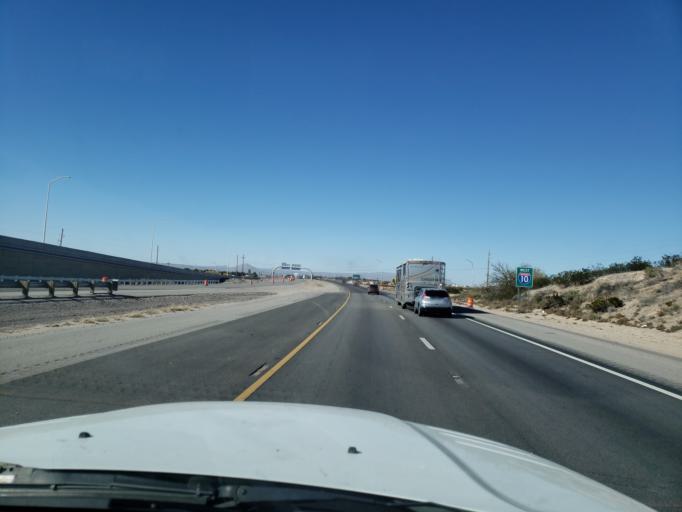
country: US
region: New Mexico
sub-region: Dona Ana County
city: University Park
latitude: 32.2630
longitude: -106.7344
